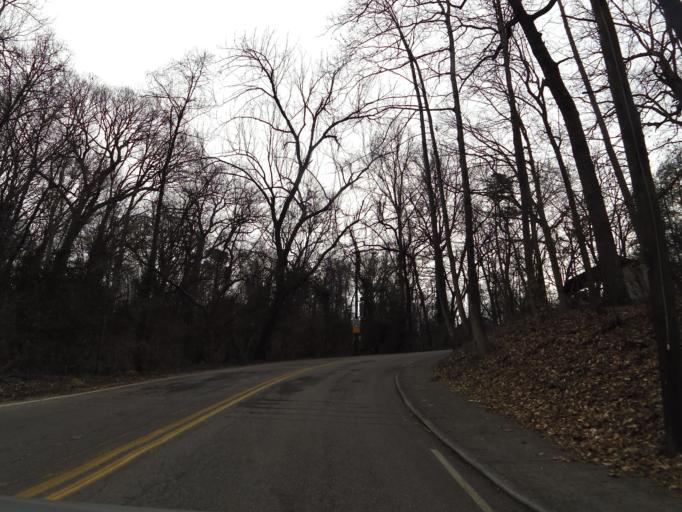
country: US
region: Tennessee
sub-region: Knox County
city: Knoxville
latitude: 35.9461
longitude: -83.9709
